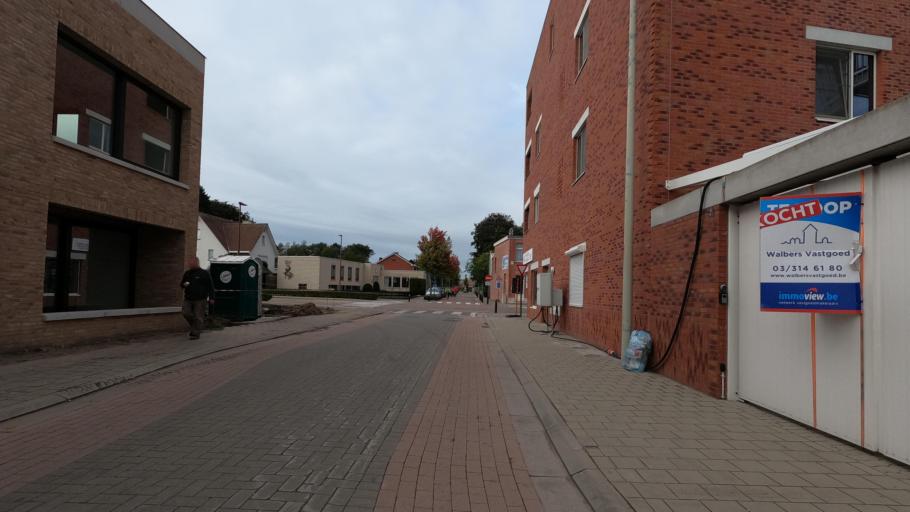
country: BE
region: Flanders
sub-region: Provincie Antwerpen
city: Rijkevorsel
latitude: 51.3492
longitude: 4.7583
